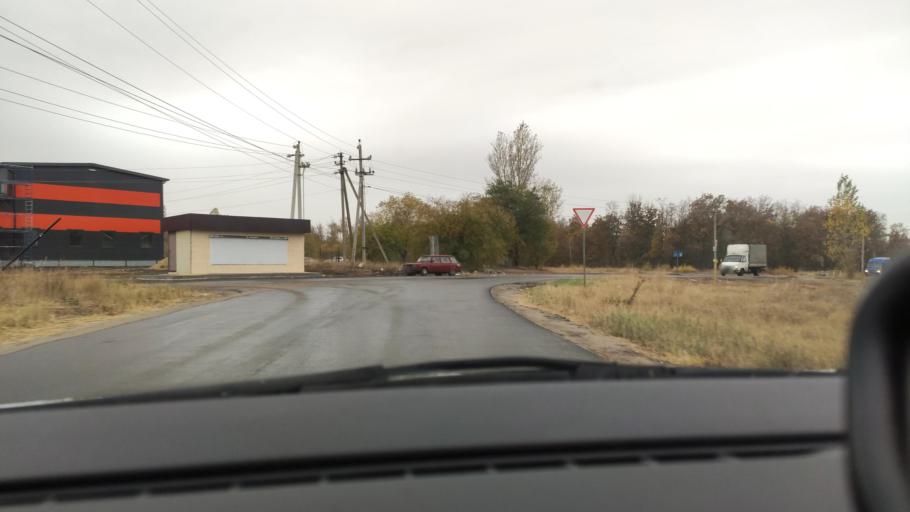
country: RU
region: Voronezj
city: Pridonskoy
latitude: 51.6407
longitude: 39.0952
